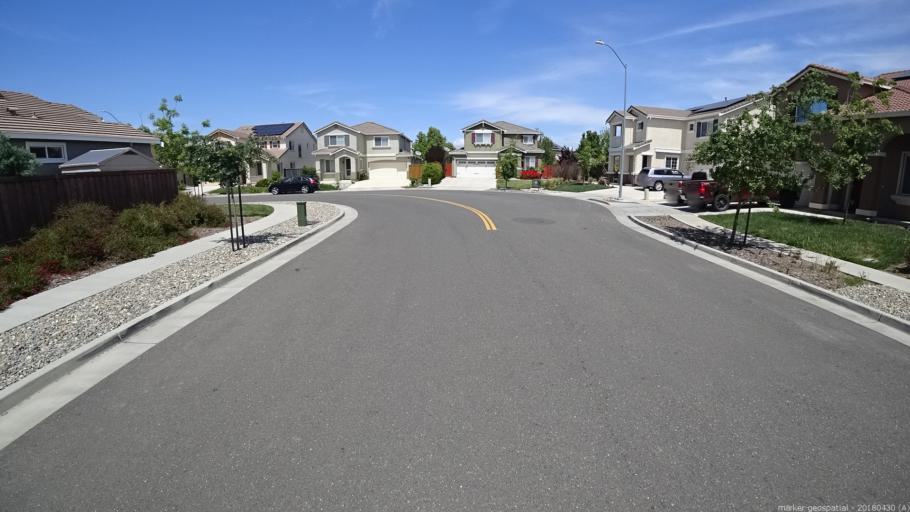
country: US
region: California
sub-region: Yolo County
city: West Sacramento
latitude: 38.5505
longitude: -121.5220
